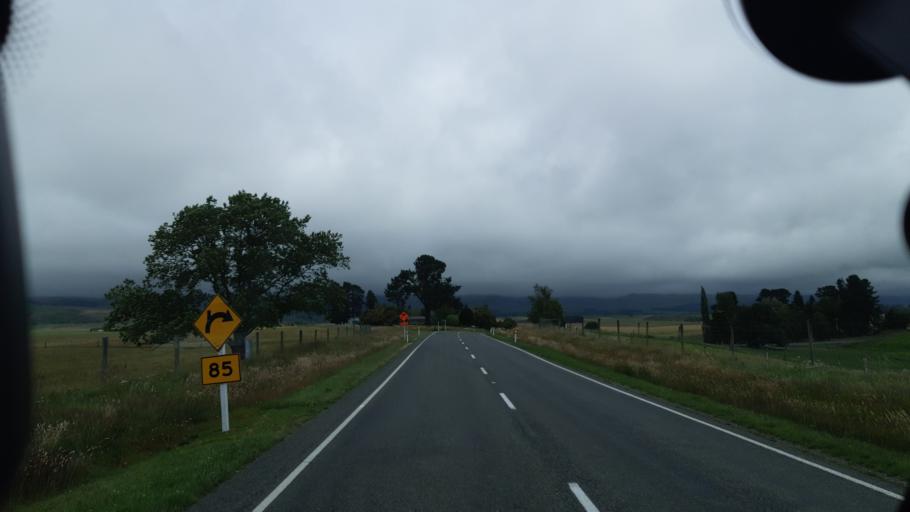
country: NZ
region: Canterbury
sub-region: Timaru District
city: Pleasant Point
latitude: -44.1471
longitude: 170.8373
